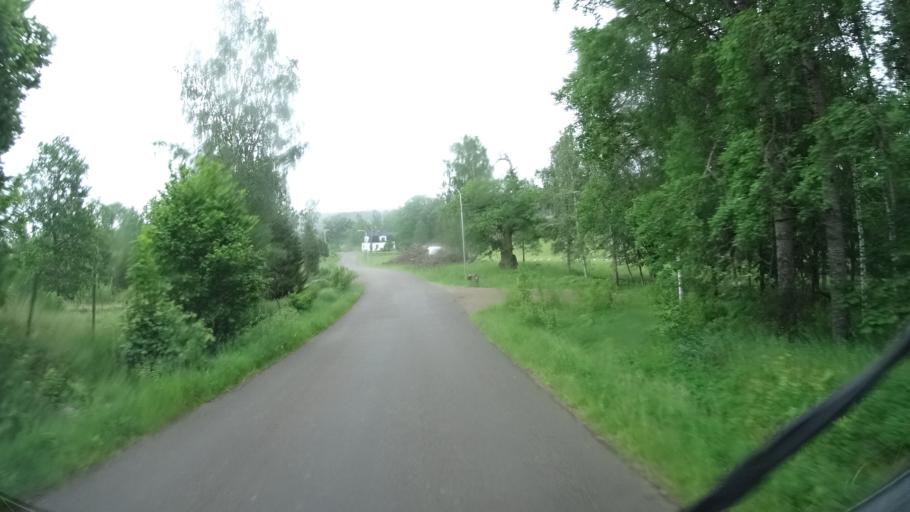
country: SE
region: Joenkoeping
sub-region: Eksjo Kommun
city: Mariannelund
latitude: 57.6781
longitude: 15.5823
